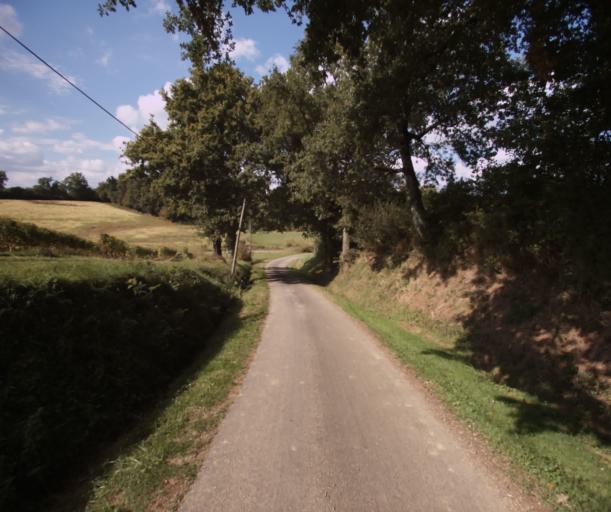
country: FR
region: Midi-Pyrenees
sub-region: Departement du Gers
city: Cazaubon
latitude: 43.9285
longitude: -0.0554
